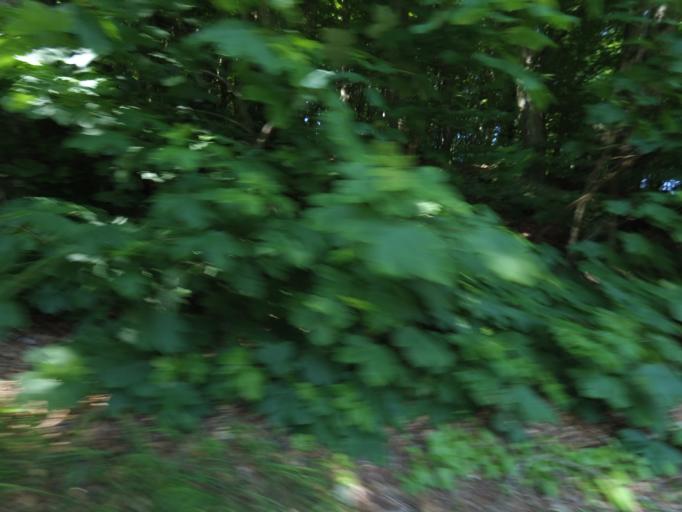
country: DK
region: Central Jutland
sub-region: Skanderborg Kommune
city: Horning
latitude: 56.1024
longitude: 10.0166
